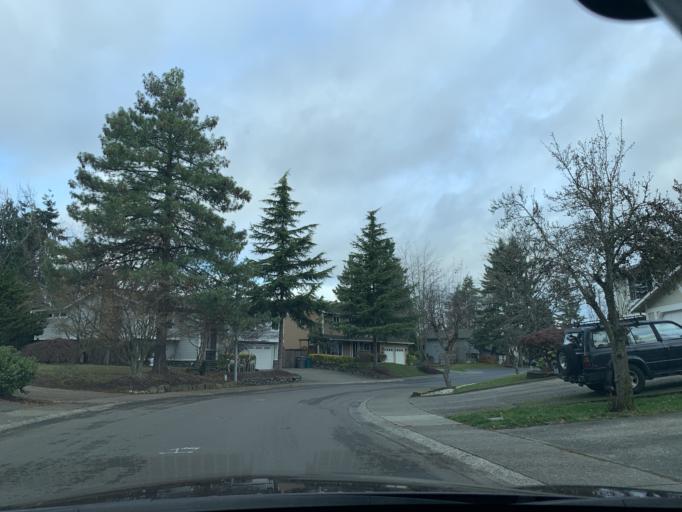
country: US
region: Washington
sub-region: King County
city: Kingsgate
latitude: 47.7336
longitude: -122.1689
